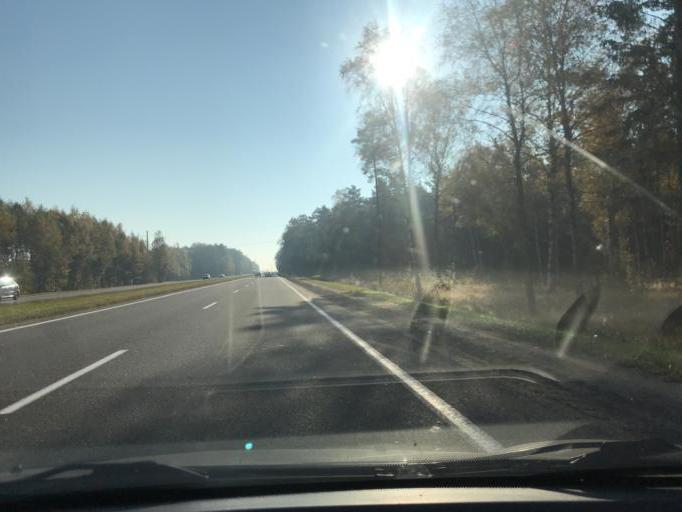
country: BY
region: Minsk
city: Dukora
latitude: 53.6265
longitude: 28.0326
